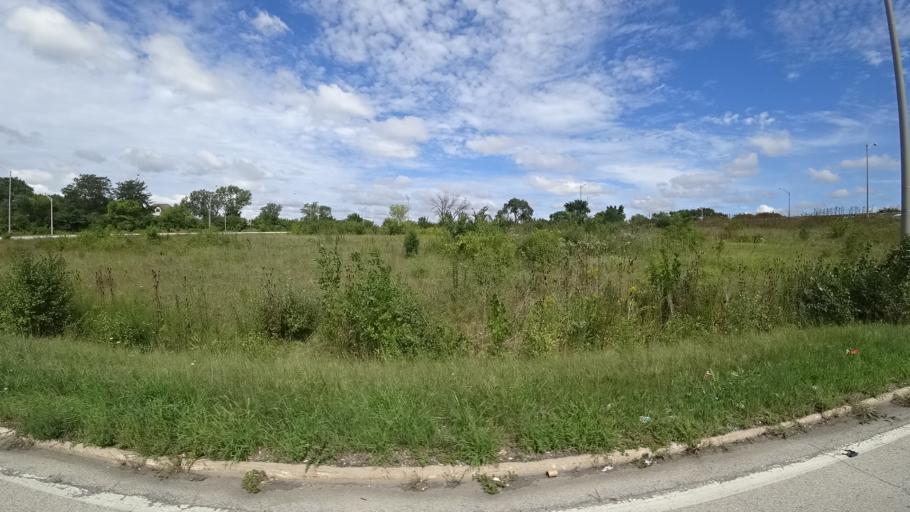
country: US
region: Illinois
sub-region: Cook County
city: Burbank
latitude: 41.7193
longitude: -87.7995
